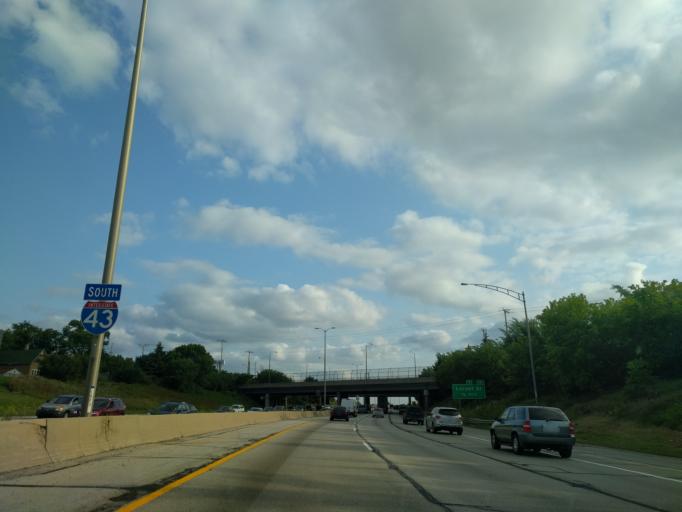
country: US
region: Wisconsin
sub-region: Milwaukee County
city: Shorewood
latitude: 43.0839
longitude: -87.9206
